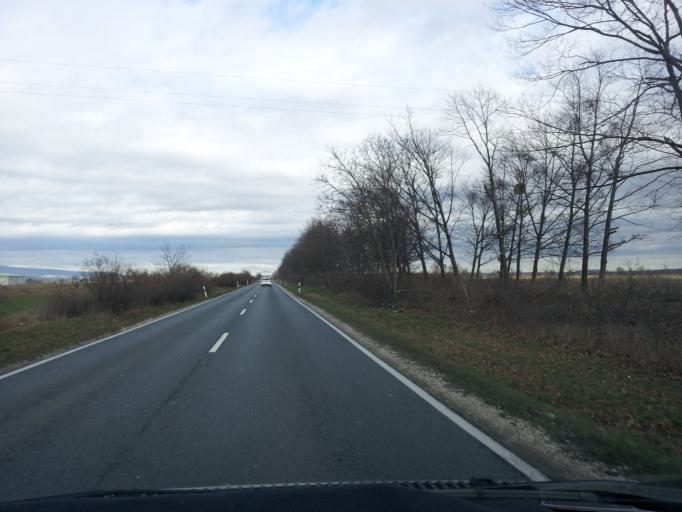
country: HU
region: Vas
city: Gencsapati
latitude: 47.2849
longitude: 16.6116
